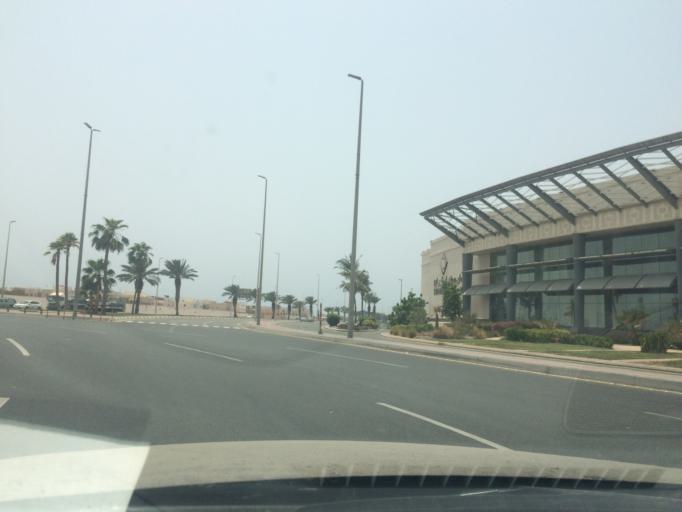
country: SA
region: Makkah
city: Jeddah
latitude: 21.6651
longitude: 39.1104
